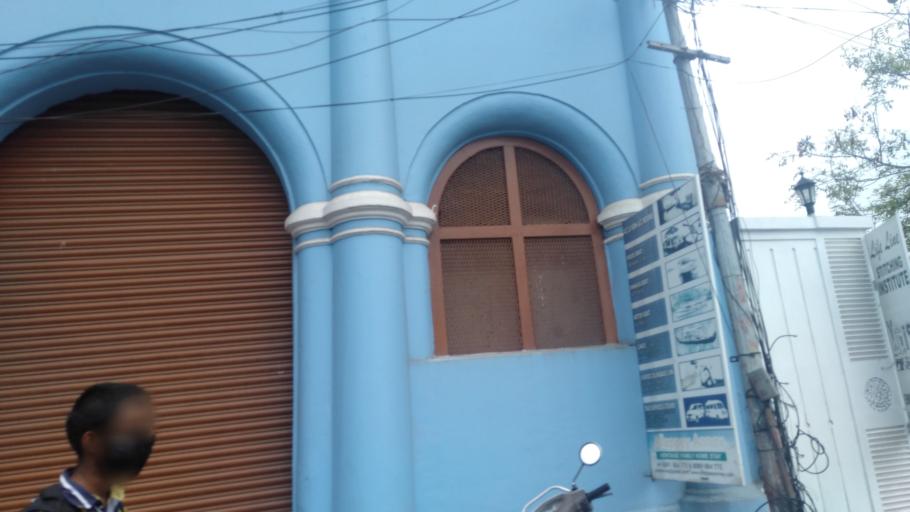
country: IN
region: Kerala
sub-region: Alappuzha
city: Alleppey
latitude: 9.4952
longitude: 76.3334
